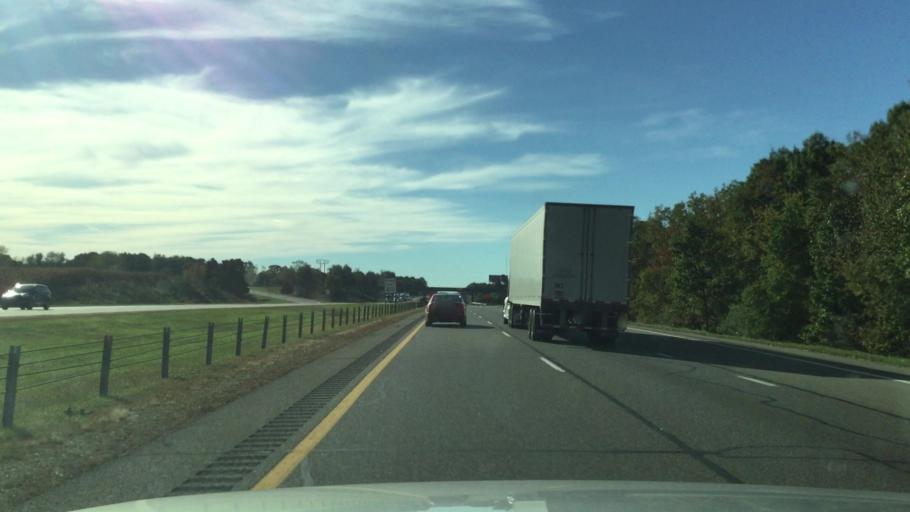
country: US
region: Michigan
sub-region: Calhoun County
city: Marshall
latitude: 42.2833
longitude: -84.8575
